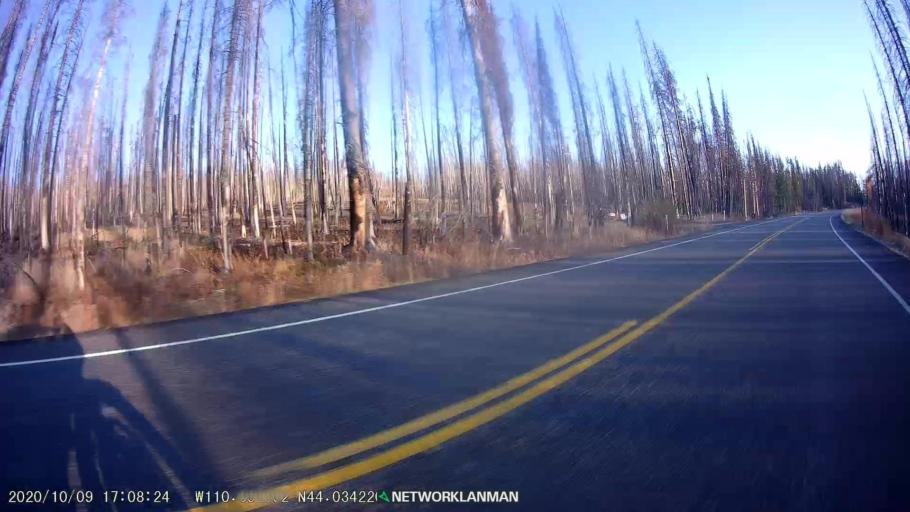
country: US
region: Idaho
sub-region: Teton County
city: Driggs
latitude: 44.0343
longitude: -110.6930
